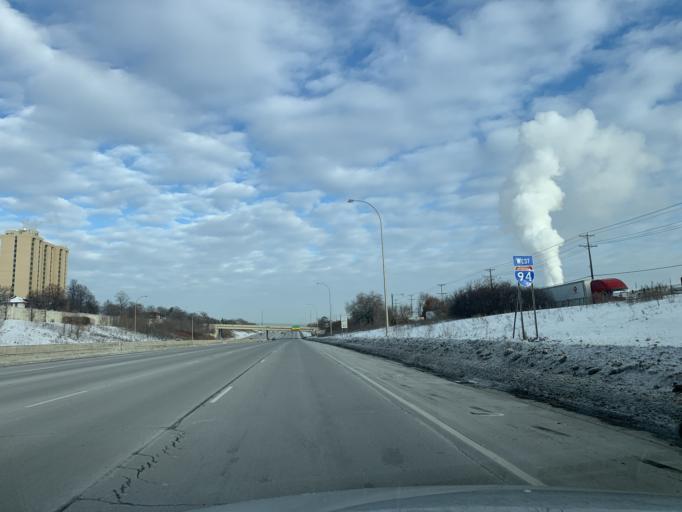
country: US
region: Minnesota
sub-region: Hennepin County
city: Minneapolis
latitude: 45.0097
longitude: -93.2824
